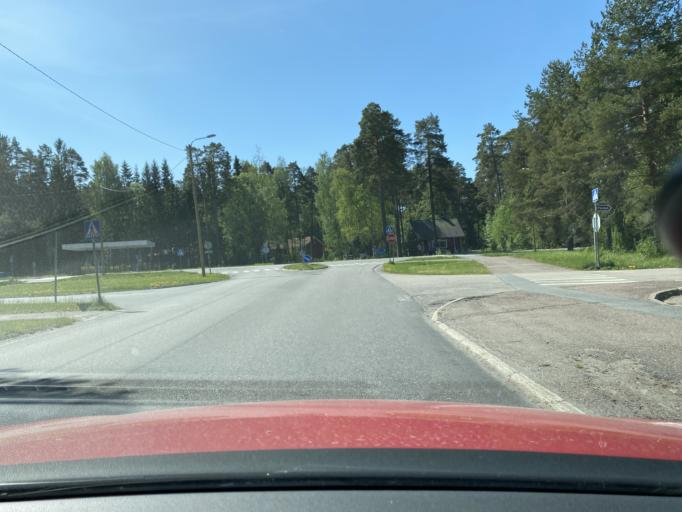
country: FI
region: Satakunta
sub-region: Rauma
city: Eura
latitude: 61.1162
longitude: 22.1607
